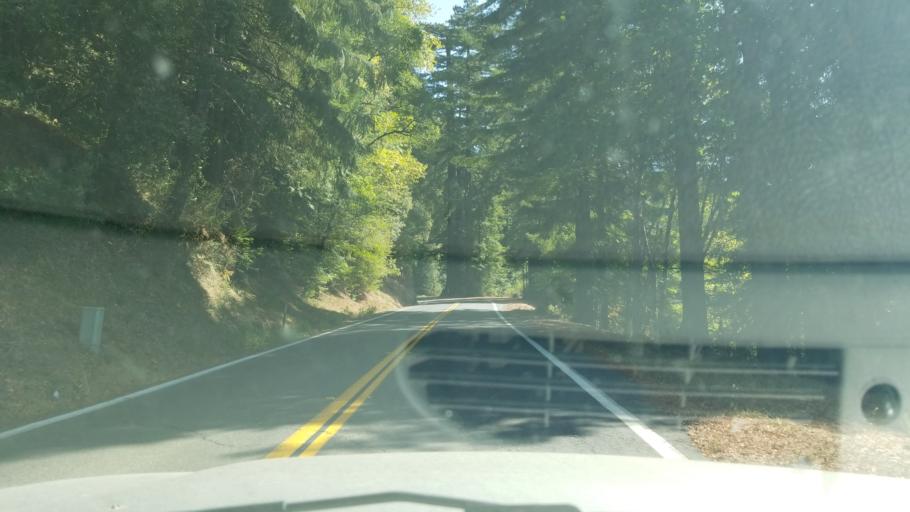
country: US
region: California
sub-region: Humboldt County
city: Redway
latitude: 40.2474
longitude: -123.8228
